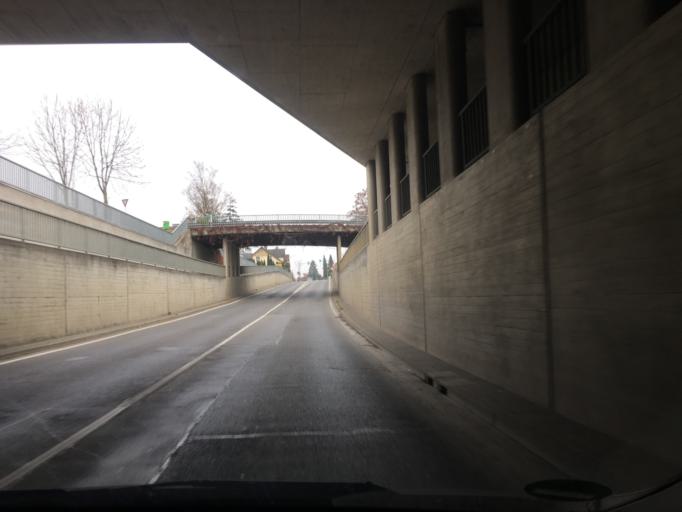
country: AT
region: Vorarlberg
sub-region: Politischer Bezirk Feldkirch
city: Altach
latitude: 47.3514
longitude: 9.6599
